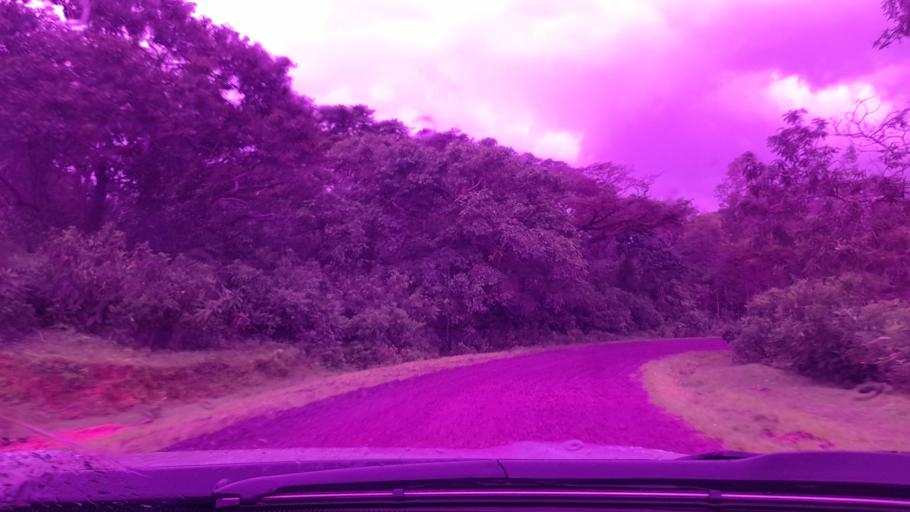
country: ET
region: Oromiya
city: Metu
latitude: 8.4344
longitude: 35.6159
